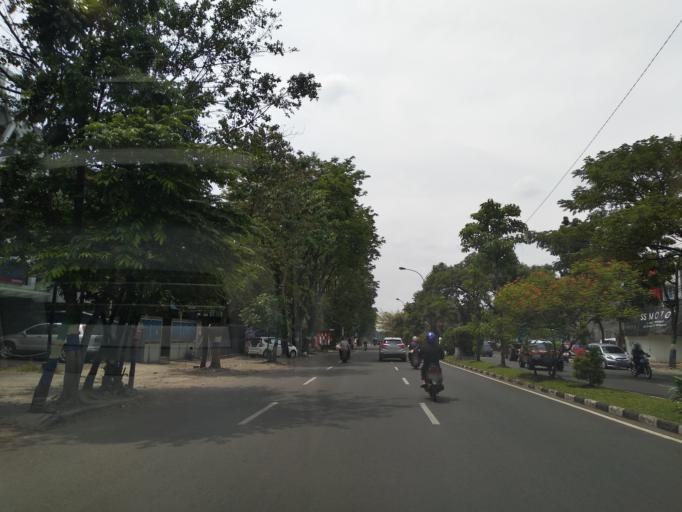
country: ID
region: West Java
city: Bandung
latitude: -6.9378
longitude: 107.6132
